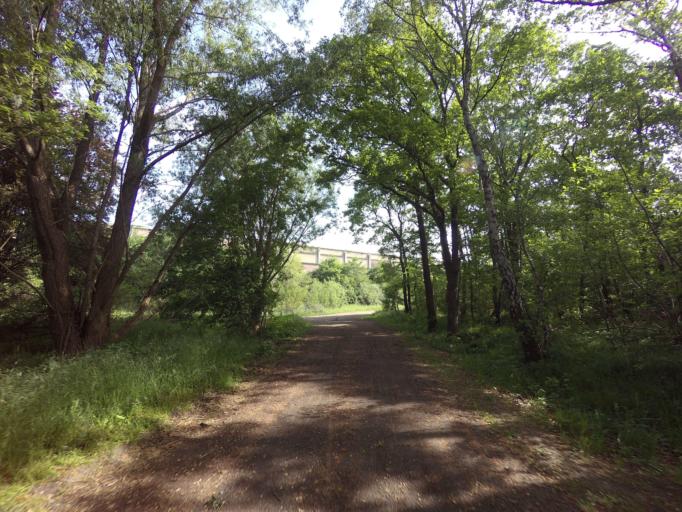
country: DE
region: Lower Saxony
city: Braunschweig
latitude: 52.3124
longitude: 10.5311
